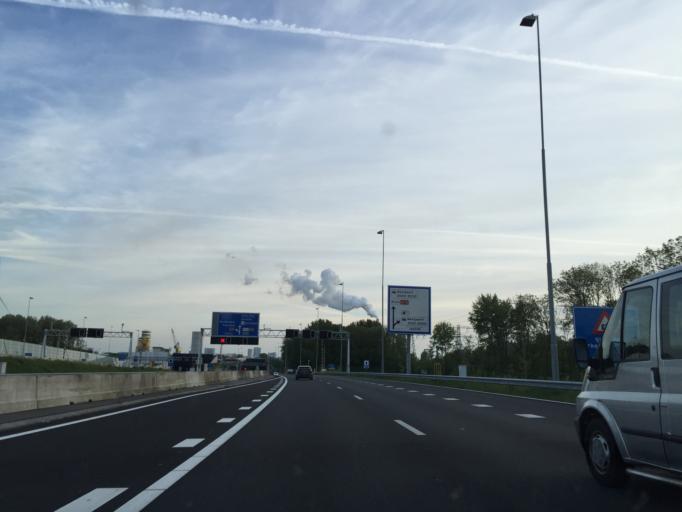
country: NL
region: North Holland
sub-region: Gemeente Landsmeer
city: Landsmeer
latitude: 52.4205
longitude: 4.8699
